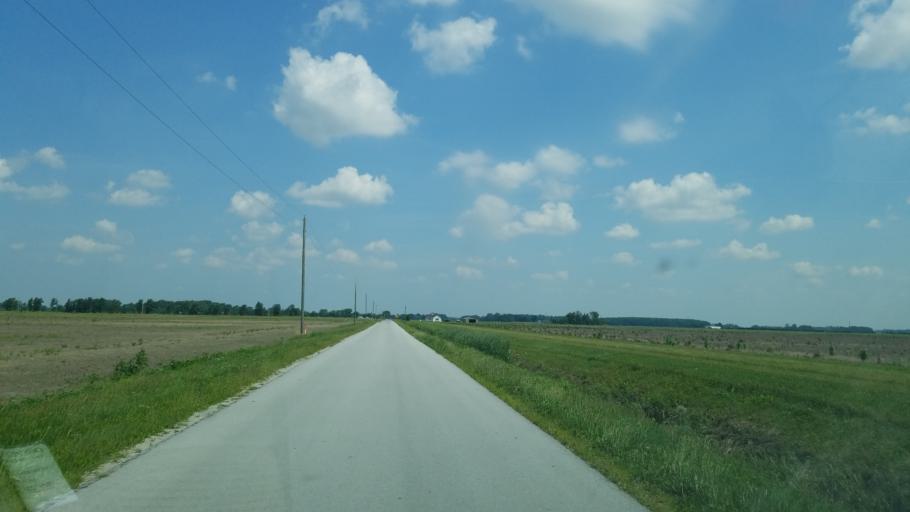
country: US
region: Ohio
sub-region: Wood County
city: Bowling Green
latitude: 41.2784
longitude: -83.6311
